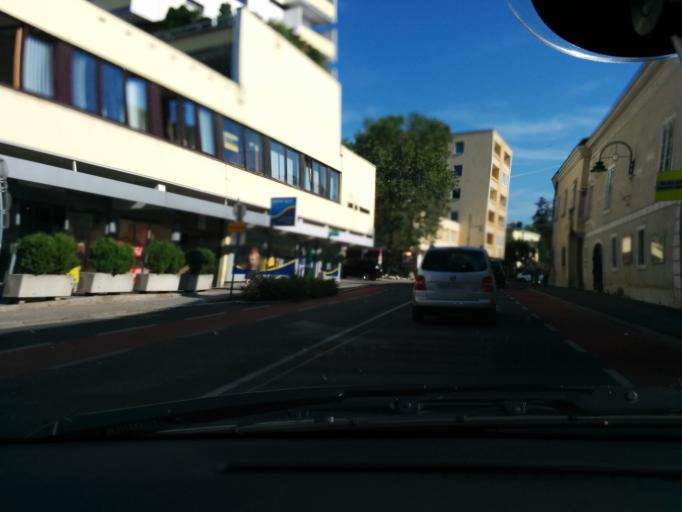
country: AT
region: Lower Austria
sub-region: Politischer Bezirk Modling
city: Modling
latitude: 48.0860
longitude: 16.2842
